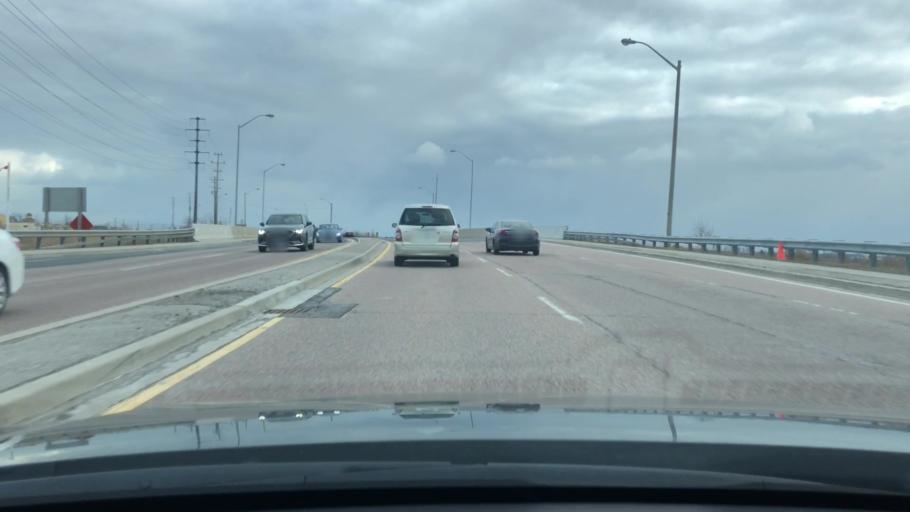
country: CA
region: Ontario
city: Markham
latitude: 43.8714
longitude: -79.2335
